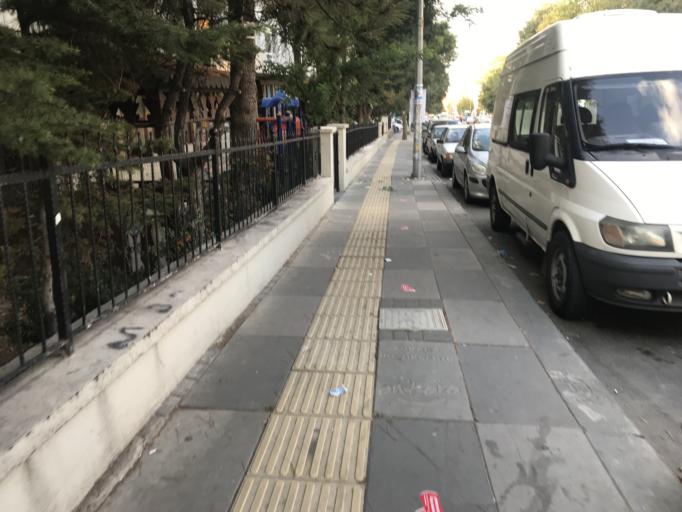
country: TR
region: Ankara
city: Ankara
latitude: 39.8750
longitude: 32.8344
